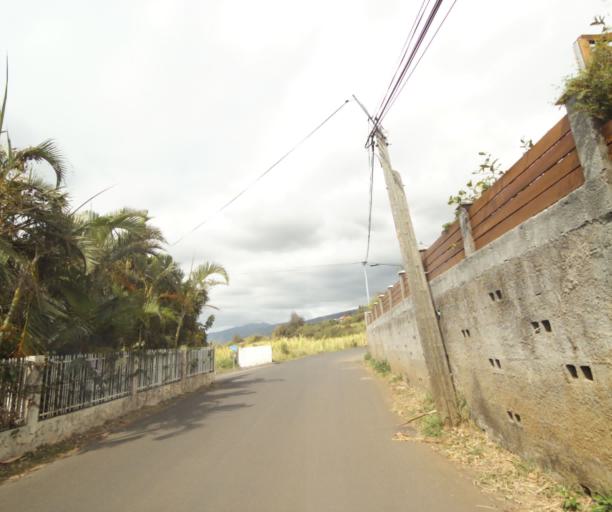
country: RE
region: Reunion
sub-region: Reunion
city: Saint-Paul
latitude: -21.0331
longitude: 55.2912
